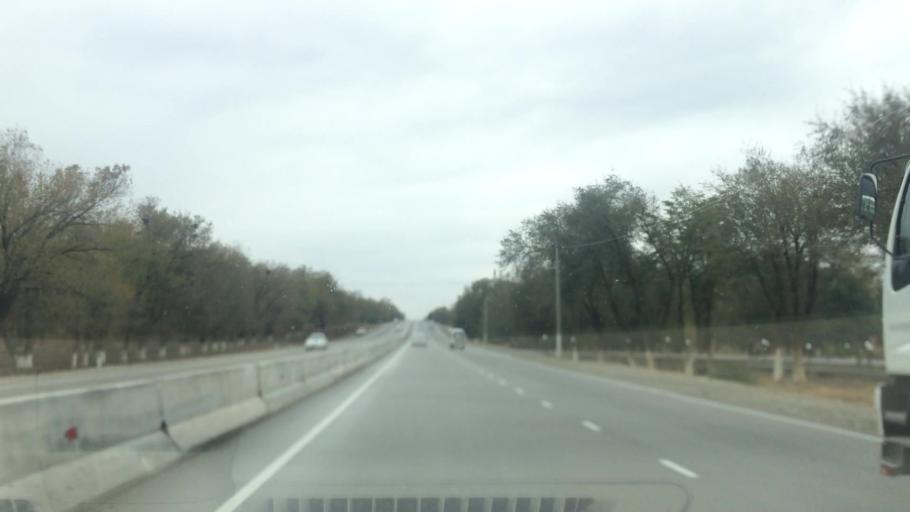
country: UZ
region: Samarqand
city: Bulung'ur
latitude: 39.8951
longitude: 67.4969
